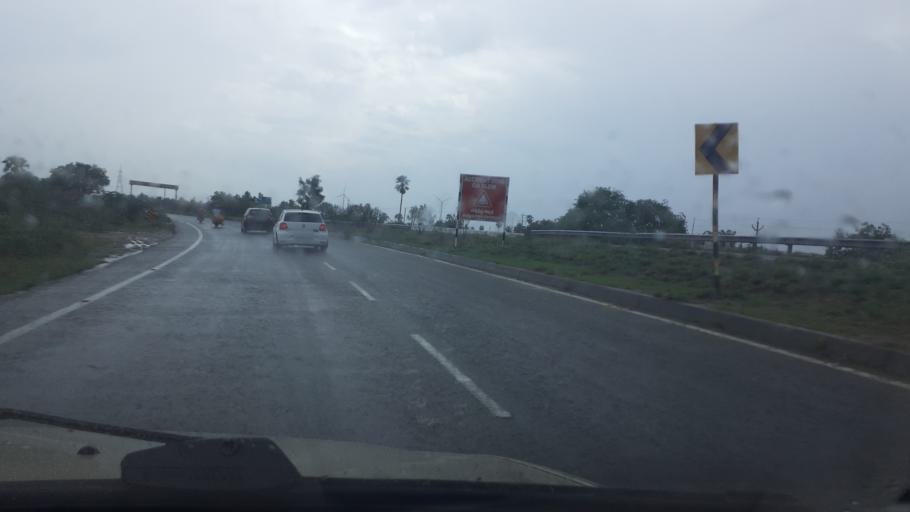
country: IN
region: Tamil Nadu
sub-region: Thoothukkudi
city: Kayattar
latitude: 8.9259
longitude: 77.7663
